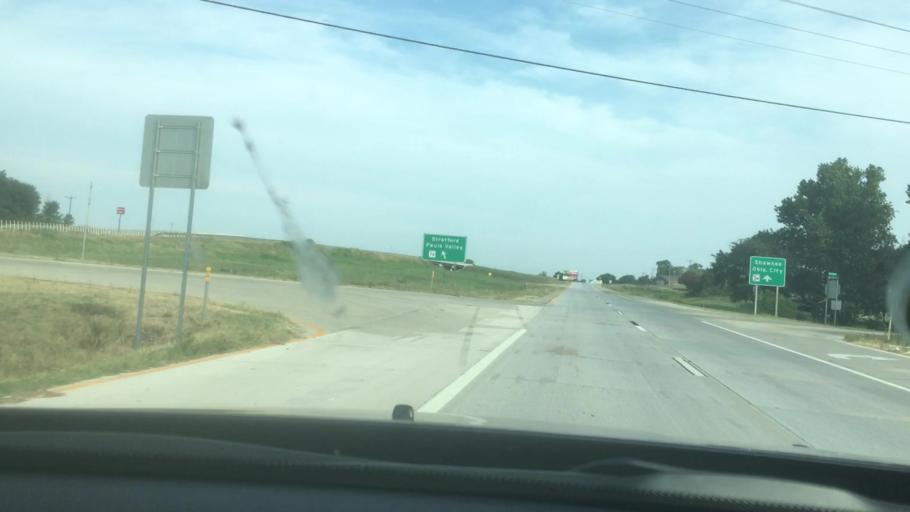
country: US
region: Oklahoma
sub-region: Pontotoc County
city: Ada
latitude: 34.7841
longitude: -96.7217
